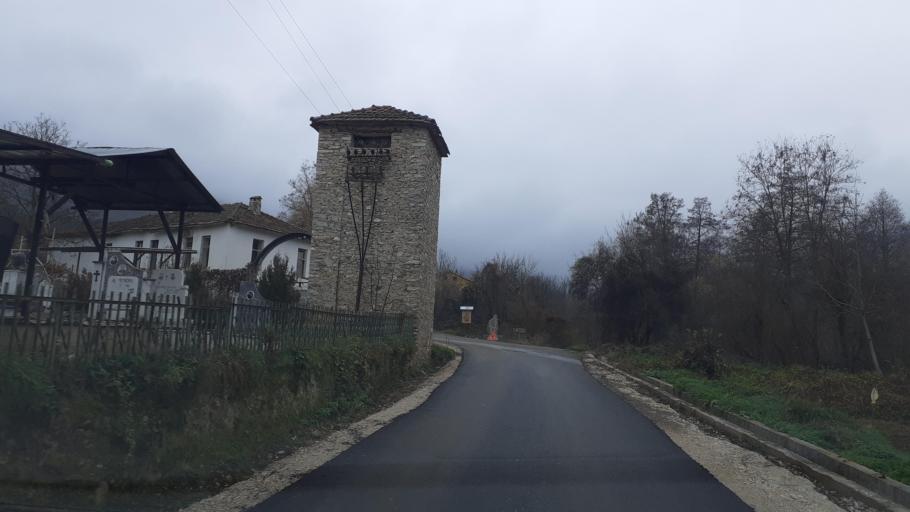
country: MK
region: Demir Hisar
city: Sopotnica
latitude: 41.2682
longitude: 21.0810
